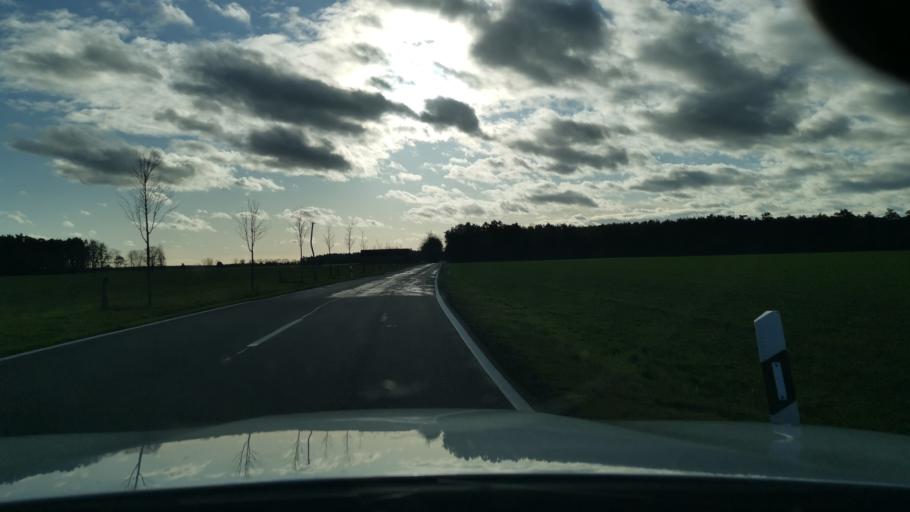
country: DE
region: Saxony-Anhalt
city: Seyda
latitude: 51.9372
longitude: 12.9161
